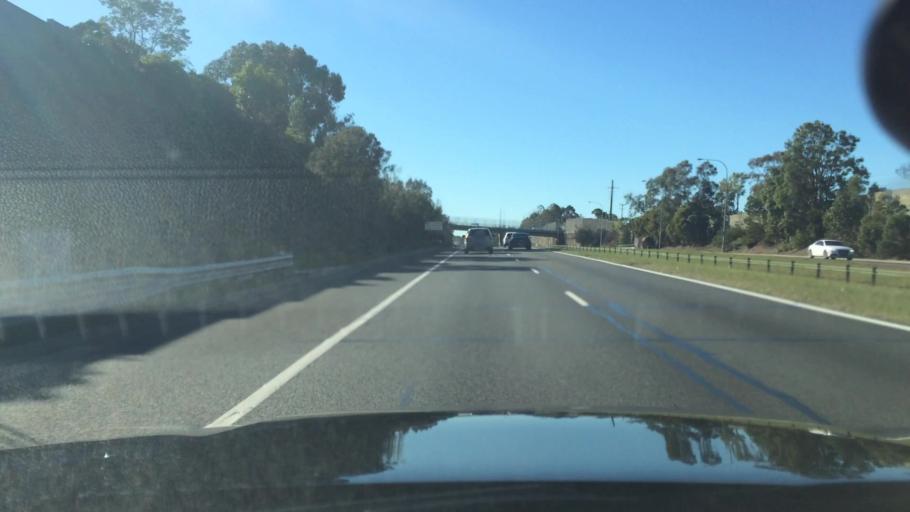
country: AU
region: New South Wales
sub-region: Parramatta
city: Northmead
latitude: -33.7716
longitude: 150.9824
